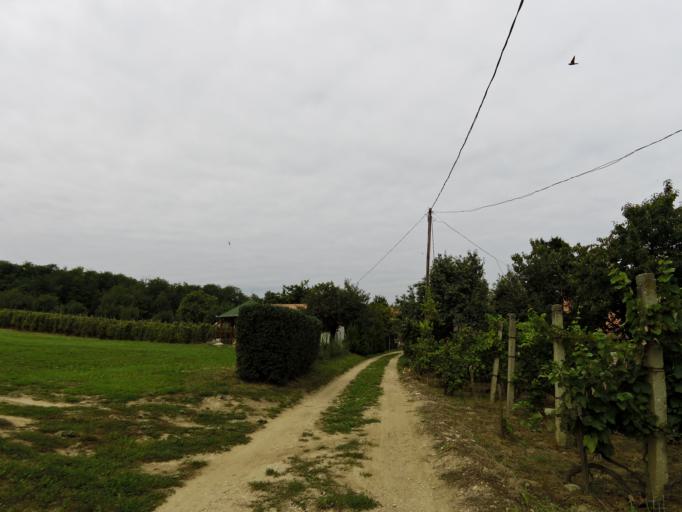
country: HU
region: Zala
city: Gyenesdias
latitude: 46.8486
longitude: 17.3304
